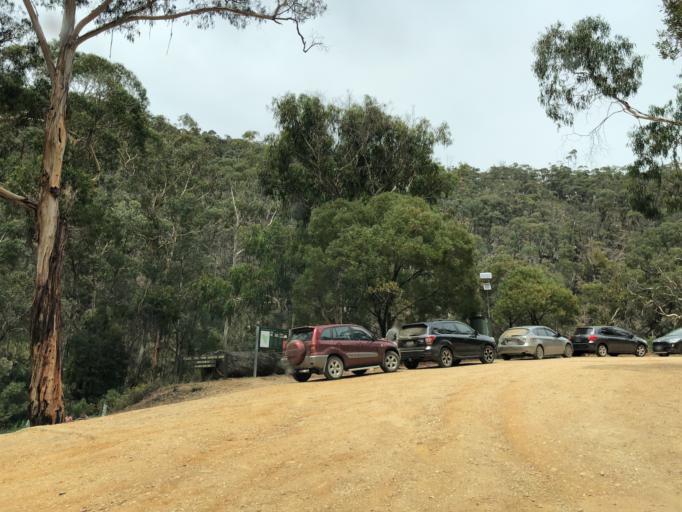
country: AU
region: Victoria
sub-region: Moorabool
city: Bacchus Marsh
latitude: -37.4961
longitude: 144.3610
